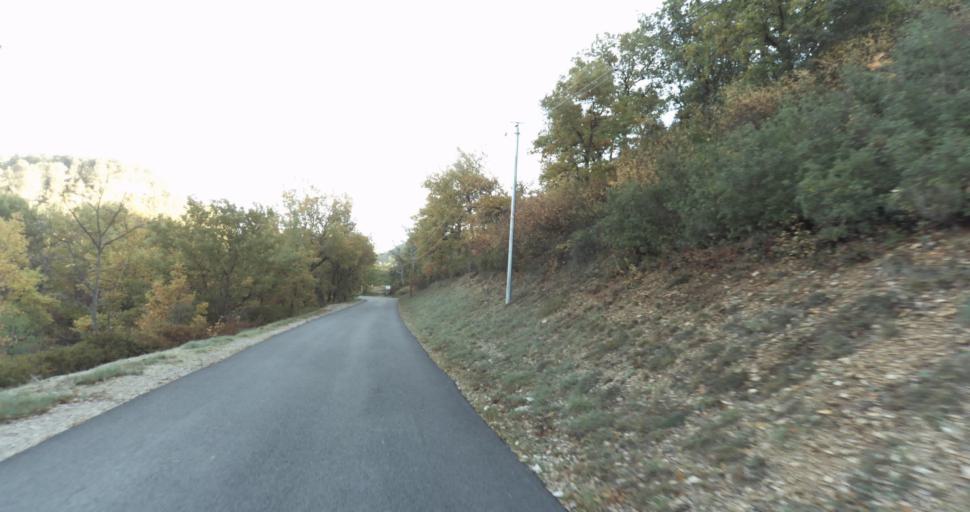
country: FR
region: Provence-Alpes-Cote d'Azur
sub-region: Departement des Bouches-du-Rhone
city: Venelles
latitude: 43.5934
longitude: 5.5161
